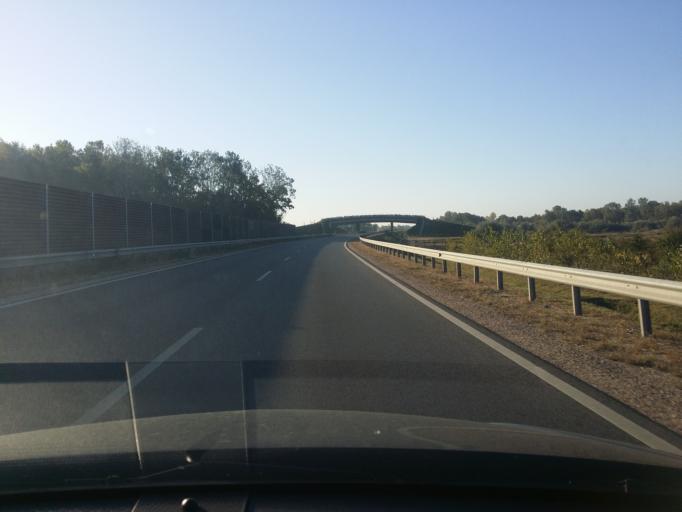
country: HU
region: Bacs-Kiskun
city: Kecskemet
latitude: 46.9365
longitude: 19.7127
